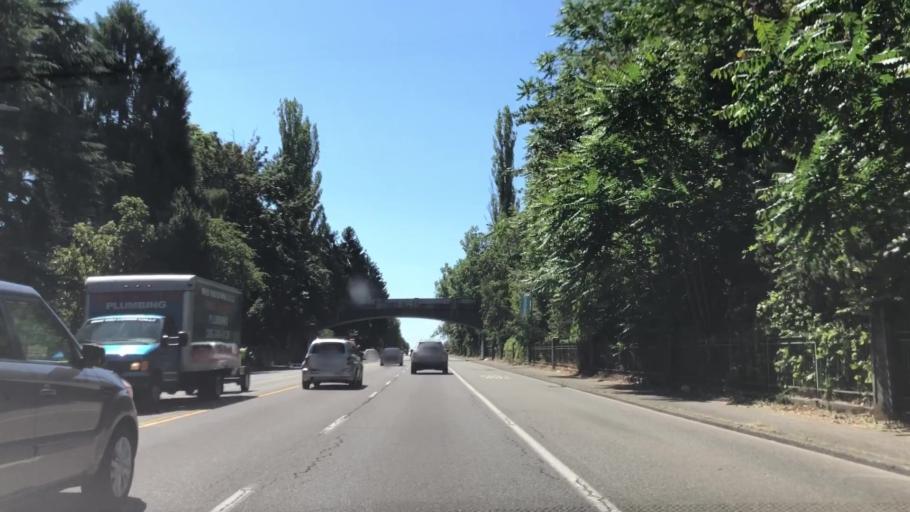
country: US
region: Washington
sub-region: King County
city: Seattle
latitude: 47.6676
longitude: -122.3472
